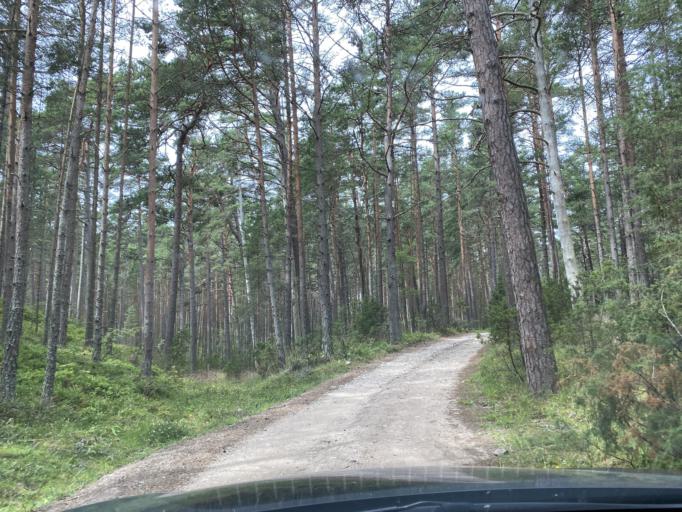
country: LV
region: Ventspils
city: Ventspils
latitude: 57.2088
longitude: 21.4197
